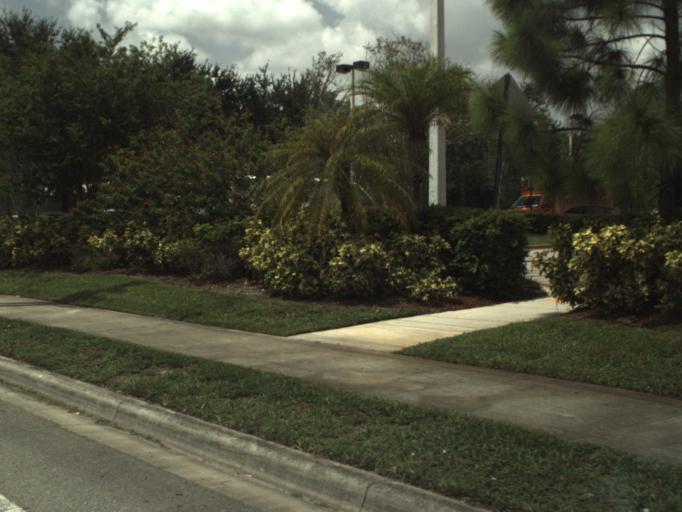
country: US
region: Florida
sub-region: Palm Beach County
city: Greenacres City
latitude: 26.6507
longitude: -80.1455
